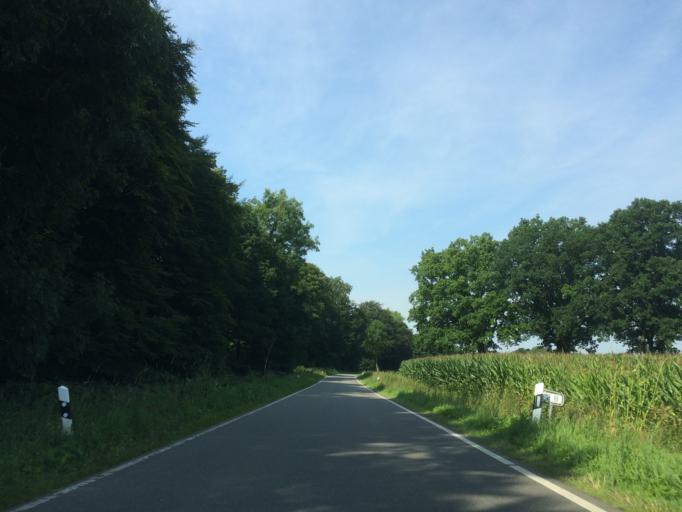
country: DE
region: Schleswig-Holstein
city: Altenhof
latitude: 54.4334
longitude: 9.8881
